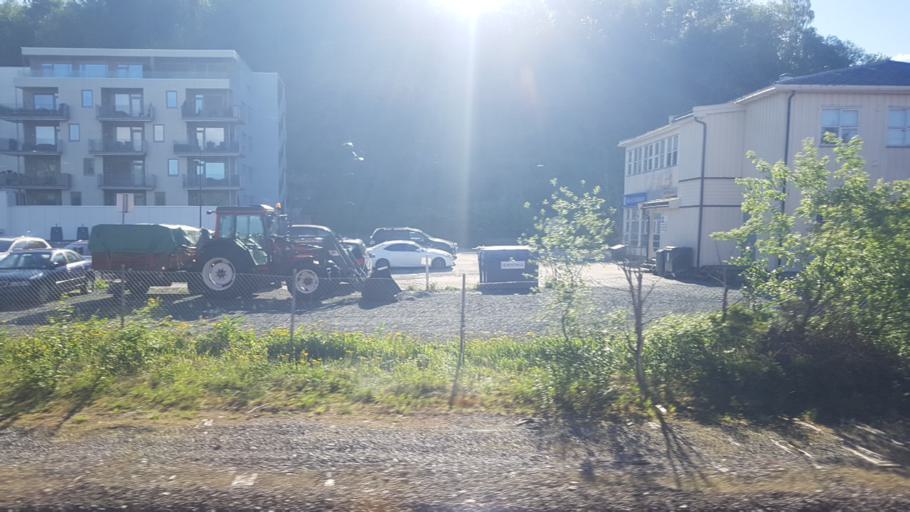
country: NO
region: Sor-Trondelag
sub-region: Melhus
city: Melhus
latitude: 63.2907
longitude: 10.2773
